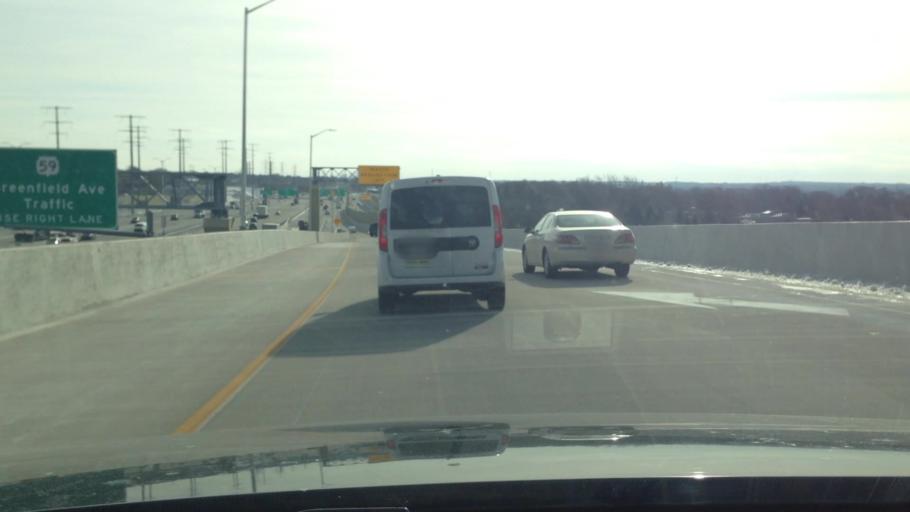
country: US
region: Wisconsin
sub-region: Milwaukee County
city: West Allis
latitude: 43.0244
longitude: -88.0368
